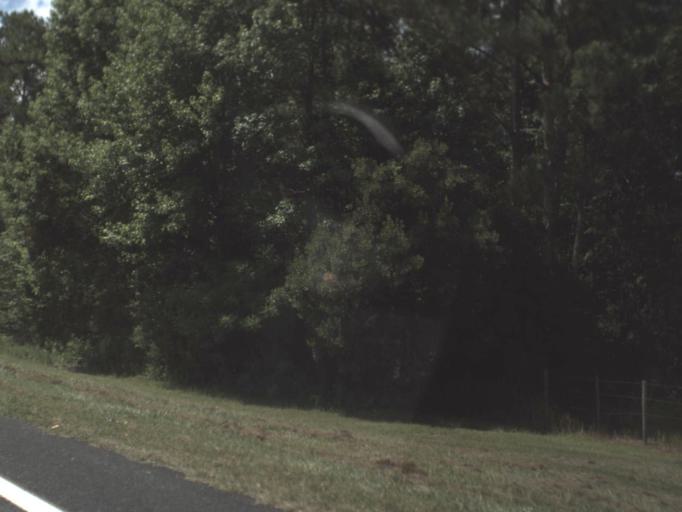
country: US
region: Florida
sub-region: Jefferson County
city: Monticello
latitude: 30.3490
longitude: -83.7931
